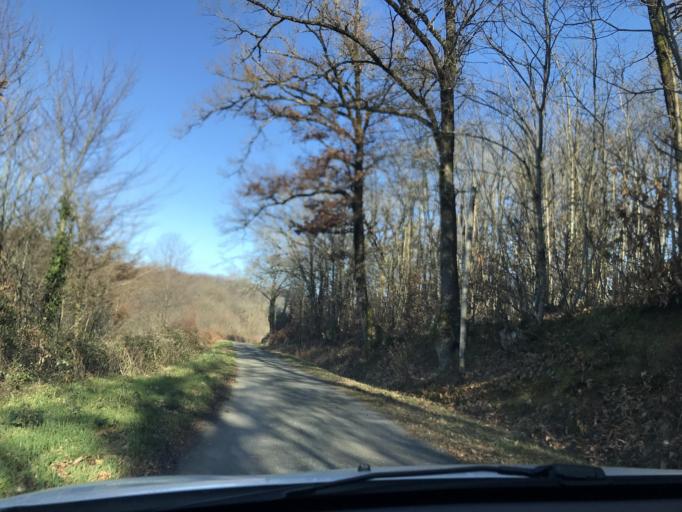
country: FR
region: Poitou-Charentes
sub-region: Departement de la Charente
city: Saint-Claud
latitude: 45.8529
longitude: 0.5269
